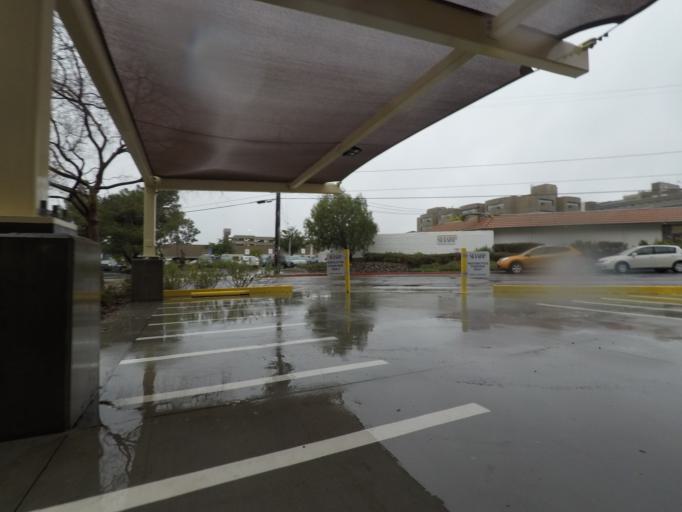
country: US
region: California
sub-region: San Diego County
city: San Diego
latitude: 32.7972
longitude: -117.1536
